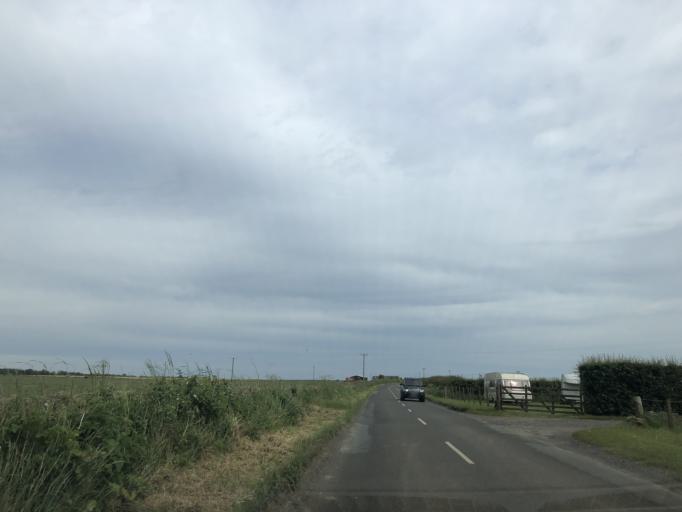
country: GB
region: Scotland
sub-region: Fife
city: Anstruther
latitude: 56.2558
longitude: -2.6993
